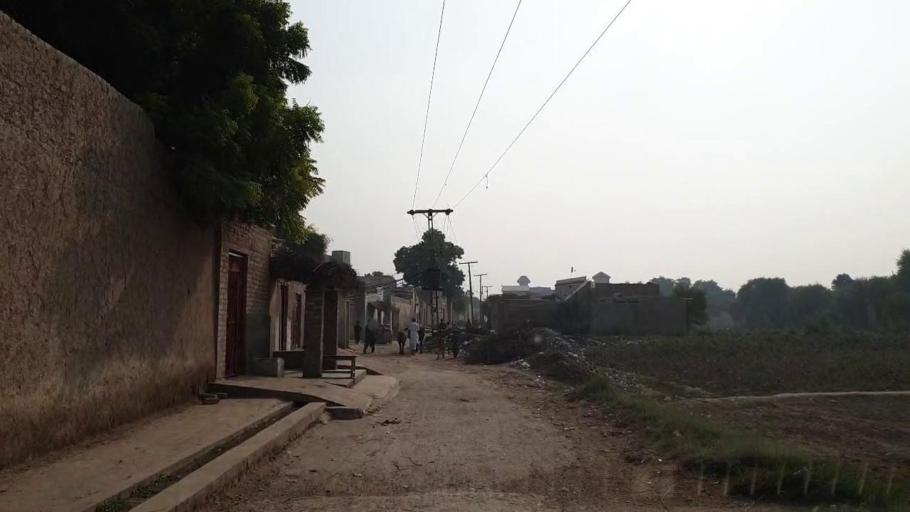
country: PK
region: Sindh
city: Bhan
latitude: 26.5805
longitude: 67.7301
